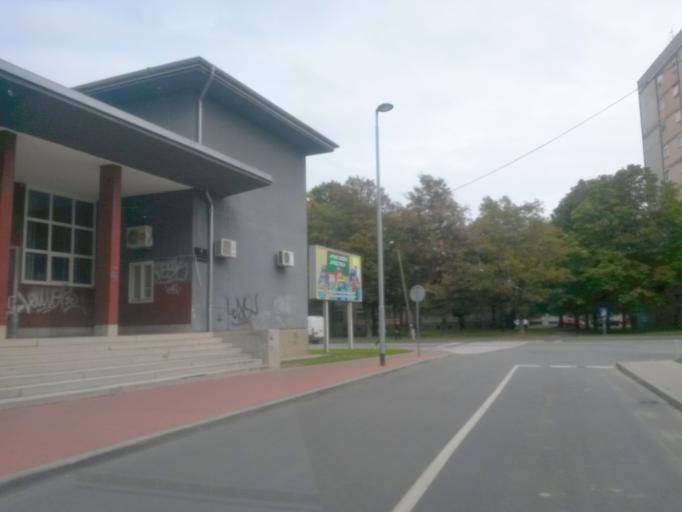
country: HR
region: Osjecko-Baranjska
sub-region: Grad Osijek
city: Osijek
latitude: 45.5561
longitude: 18.6955
